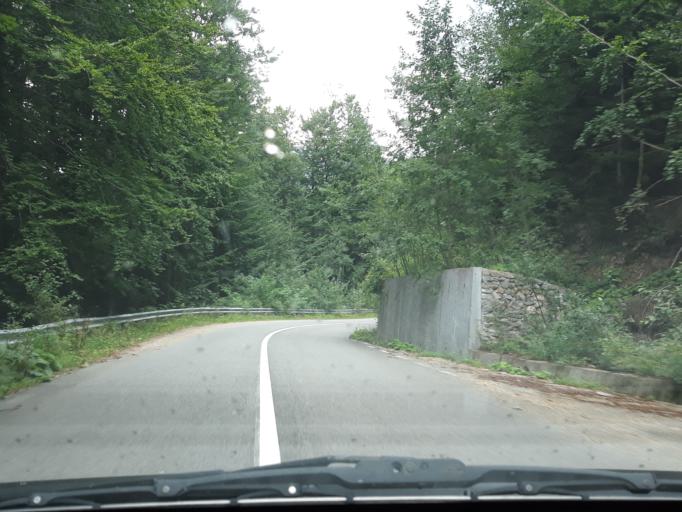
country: RO
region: Bihor
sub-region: Comuna Pietroasa
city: Pietroasa
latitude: 46.5950
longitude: 22.6710
